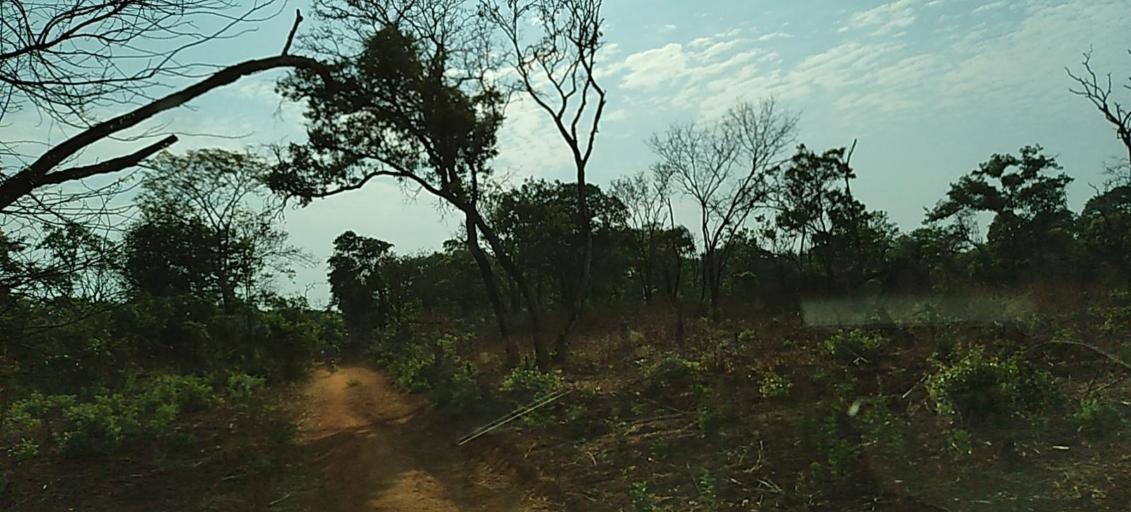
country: ZM
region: Copperbelt
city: Kalulushi
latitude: -12.9632
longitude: 27.7104
